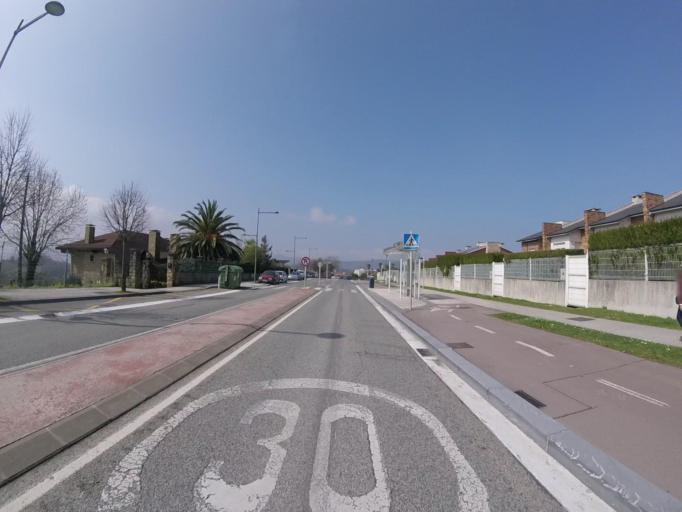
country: ES
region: Basque Country
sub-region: Provincia de Guipuzcoa
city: Hernani
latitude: 43.2871
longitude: -1.9875
